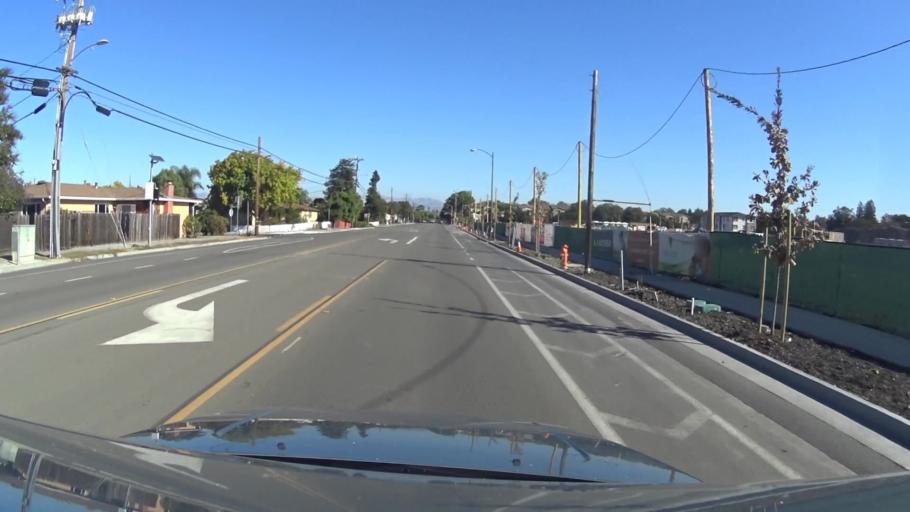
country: US
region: California
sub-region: Santa Clara County
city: Sunnyvale
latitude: 37.3883
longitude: -122.0070
